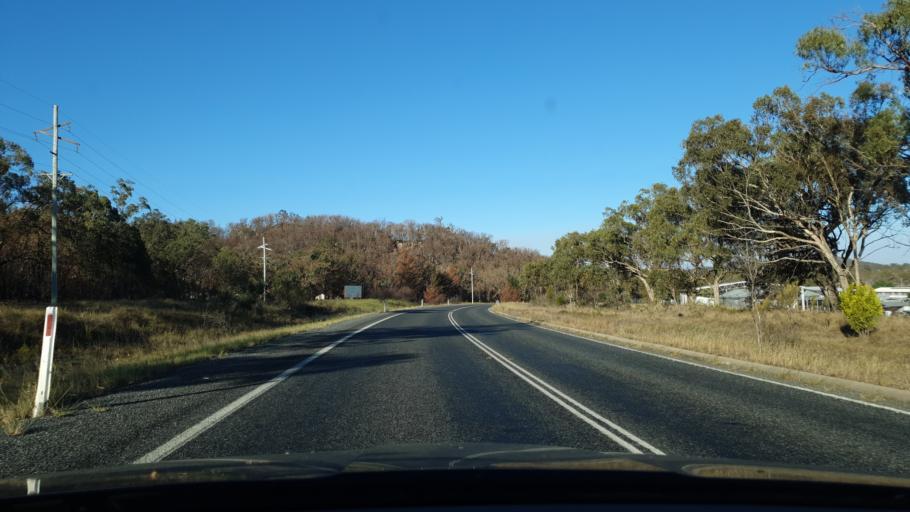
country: AU
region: Queensland
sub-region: Southern Downs
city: Stanthorpe
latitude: -28.6456
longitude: 151.9266
